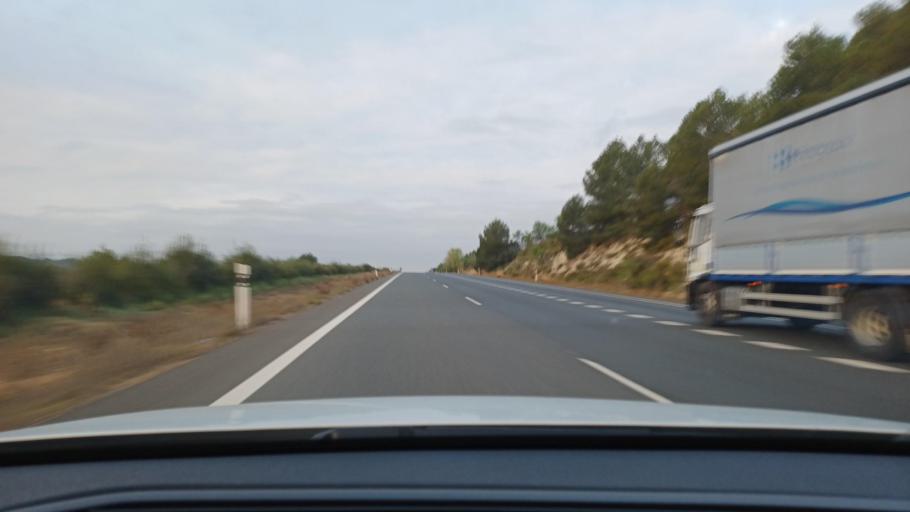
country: ES
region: Valencia
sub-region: Provincia de Valencia
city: Mogente
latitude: 38.8659
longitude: -0.7887
